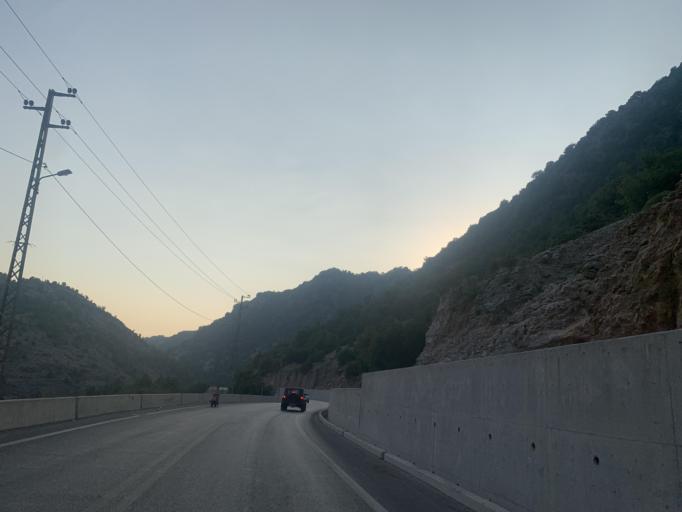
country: LB
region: Liban-Nord
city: Amioun
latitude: 34.1360
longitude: 35.8301
